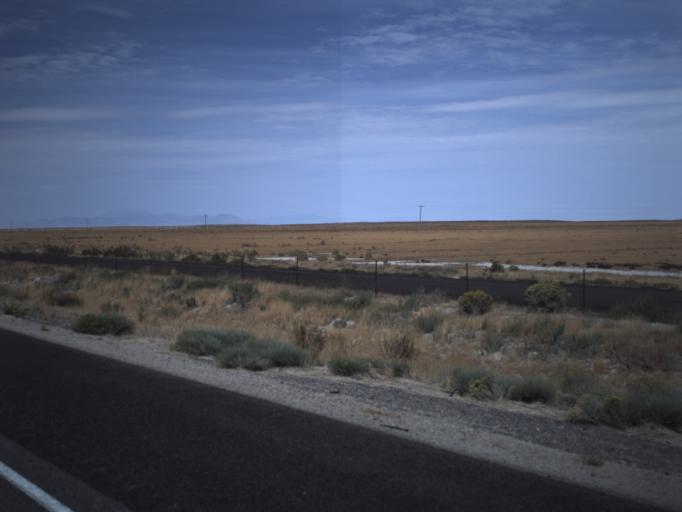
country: US
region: Utah
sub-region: Tooele County
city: Grantsville
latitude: 40.7268
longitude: -113.2091
